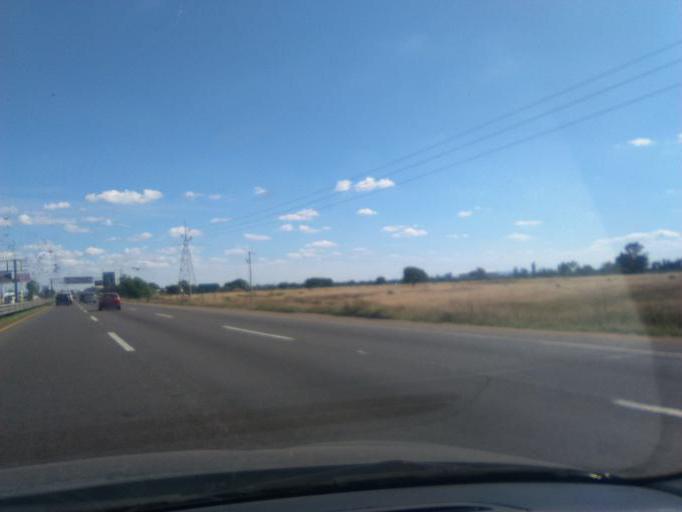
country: MX
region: Guanajuato
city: Silao
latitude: 20.9648
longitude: -101.4550
